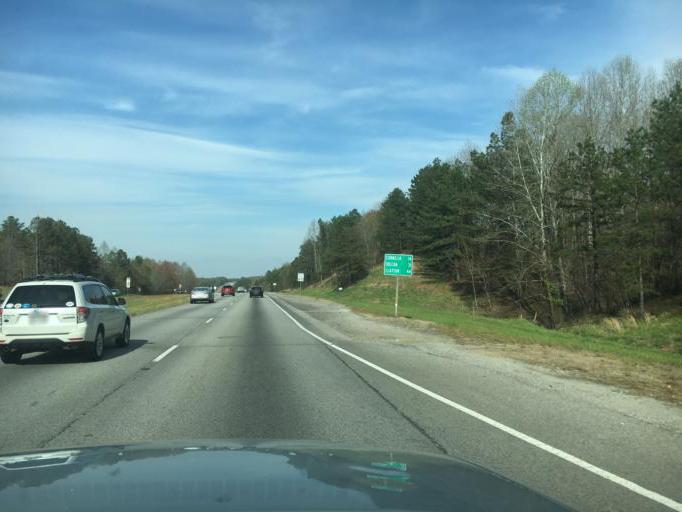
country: US
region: Georgia
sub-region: Hall County
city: Lula
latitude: 34.3956
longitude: -83.6900
